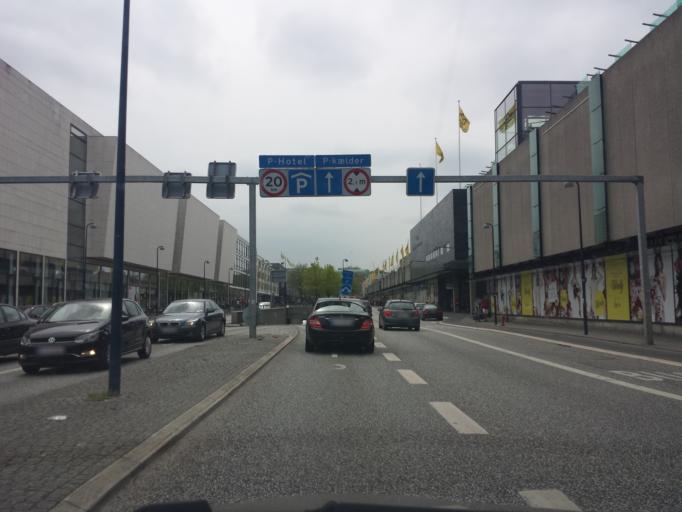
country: DK
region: Capital Region
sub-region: Lyngby-Tarbaek Kommune
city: Kongens Lyngby
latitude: 55.7720
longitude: 12.5082
